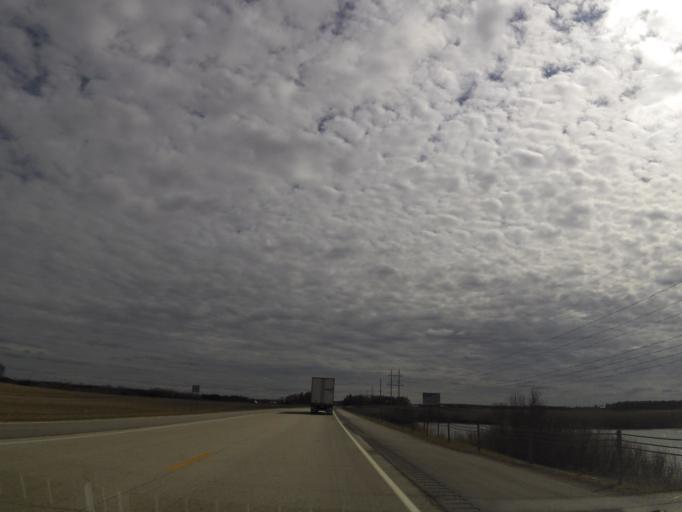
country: US
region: Minnesota
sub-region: Fillmore County
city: Spring Valley
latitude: 43.6450
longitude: -92.3894
